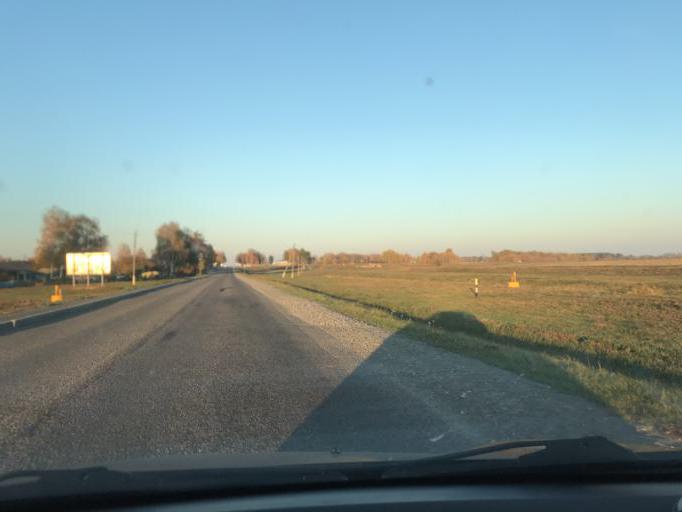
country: BY
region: Gomel
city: Brahin
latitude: 51.8056
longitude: 30.2764
